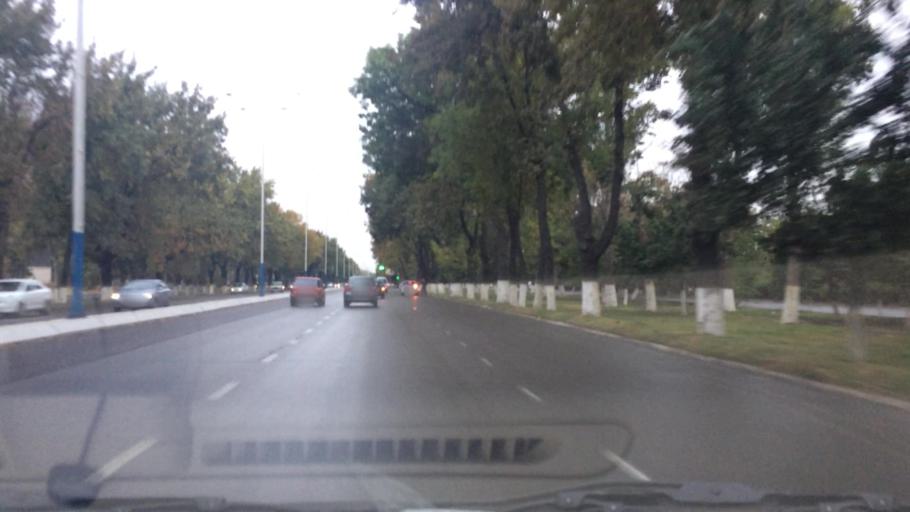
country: UZ
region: Toshkent Shahri
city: Tashkent
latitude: 41.2668
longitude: 69.2000
